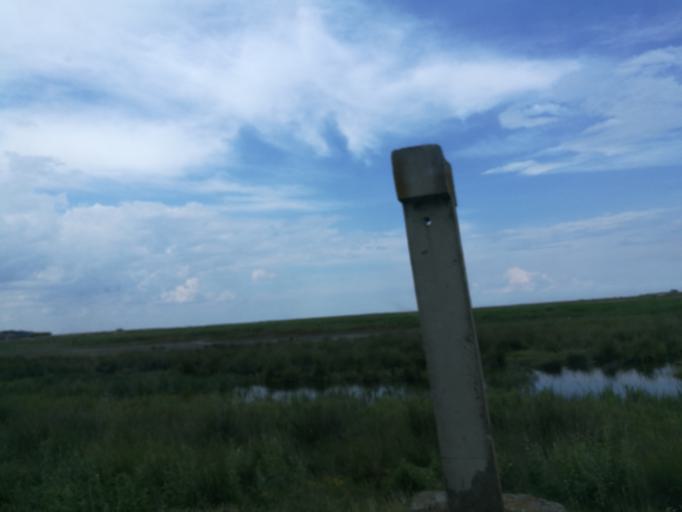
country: RO
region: Constanta
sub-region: Comuna Sacele
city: Sacele
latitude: 44.4449
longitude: 28.7439
